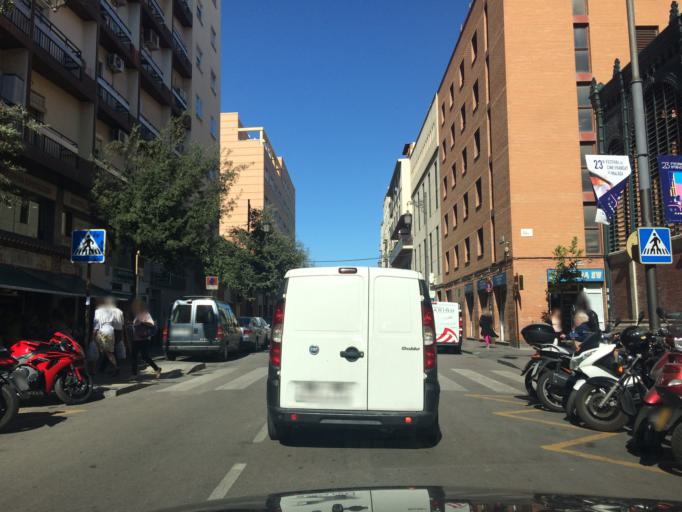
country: ES
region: Andalusia
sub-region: Provincia de Malaga
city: Malaga
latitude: 36.7183
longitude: -4.4245
